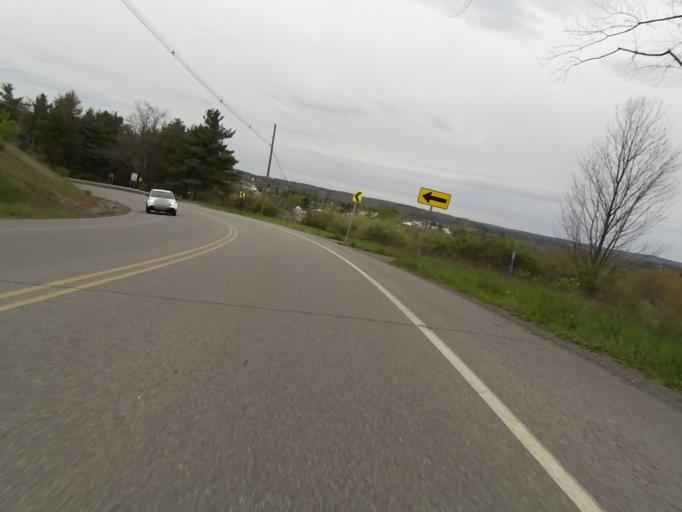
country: US
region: Pennsylvania
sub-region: Clearfield County
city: Troy
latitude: 40.9044
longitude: -78.2074
